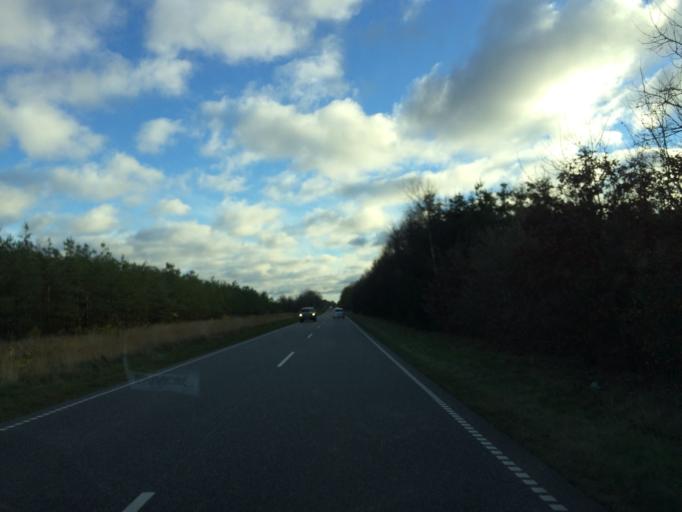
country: DK
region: Central Jutland
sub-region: Herning Kommune
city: Kibaek
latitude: 55.9418
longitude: 8.8892
